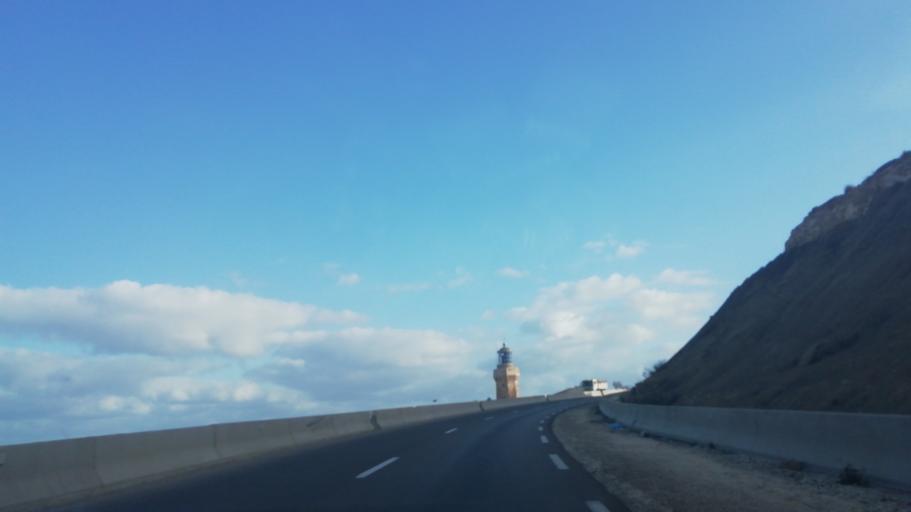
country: DZ
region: Mostaganem
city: Mostaganem
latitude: 36.1113
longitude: 0.2260
